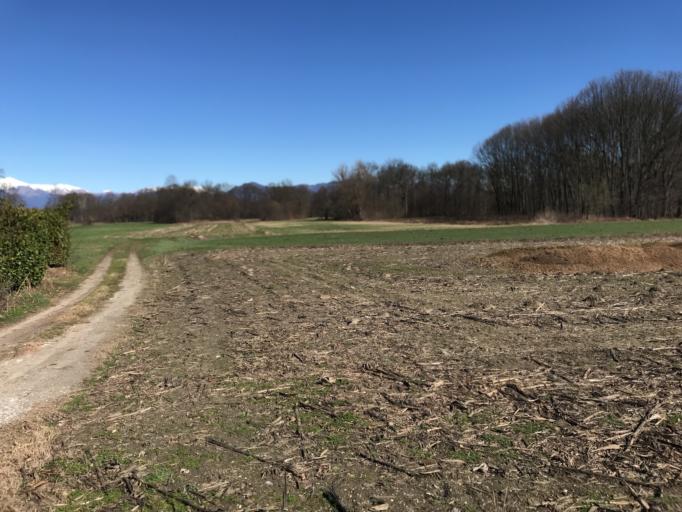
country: IT
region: Lombardy
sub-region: Provincia di Varese
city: Taino
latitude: 45.7762
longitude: 8.6054
